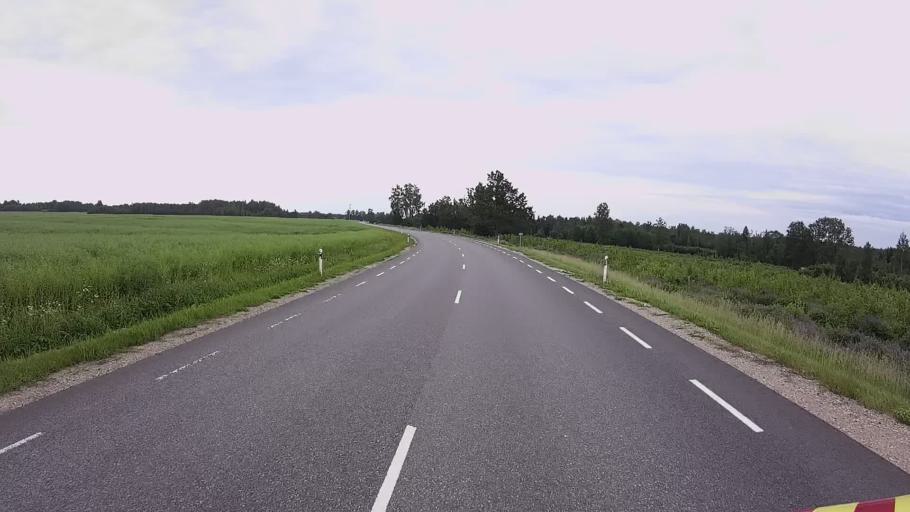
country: EE
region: Viljandimaa
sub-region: Karksi vald
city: Karksi-Nuia
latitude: 58.1688
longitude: 25.5803
